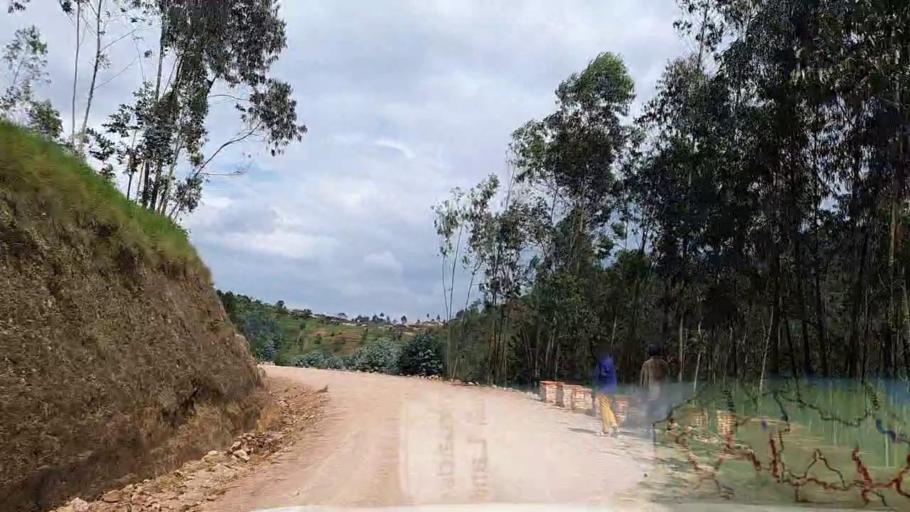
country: RW
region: Southern Province
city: Nzega
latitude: -2.3387
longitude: 29.4390
